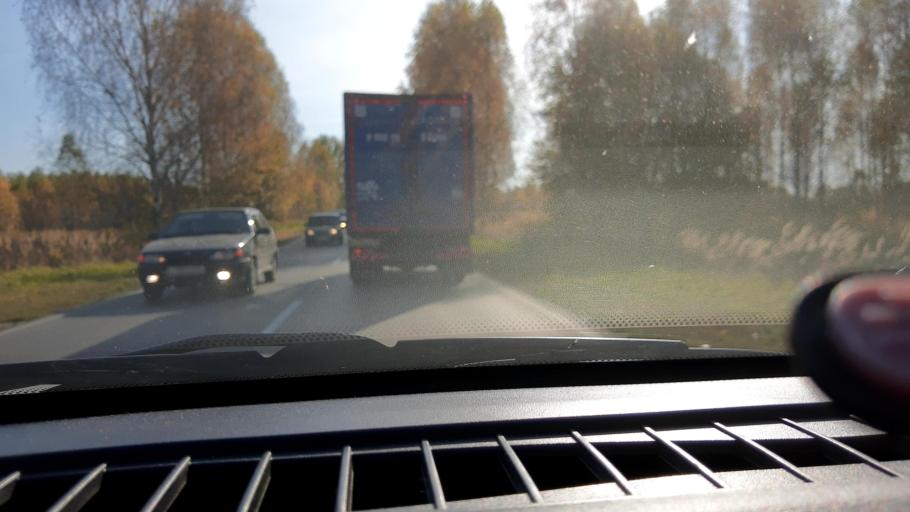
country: RU
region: Nizjnij Novgorod
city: Neklyudovo
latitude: 56.4709
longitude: 43.8880
